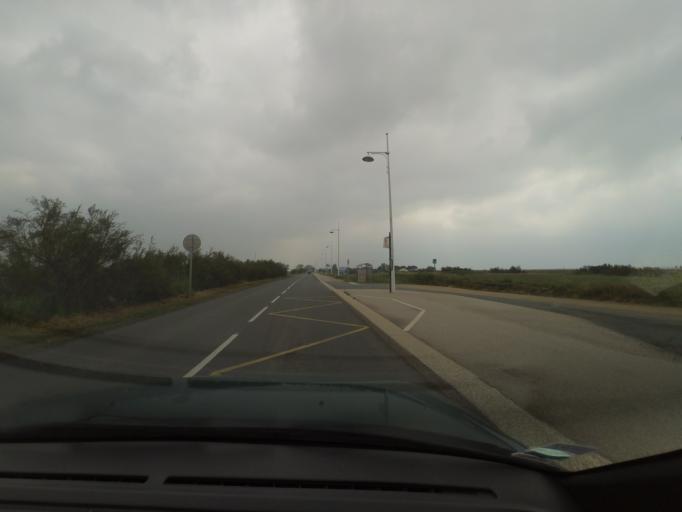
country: FR
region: Pays de la Loire
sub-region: Departement de la Vendee
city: Angles
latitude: 46.3428
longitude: -1.3431
